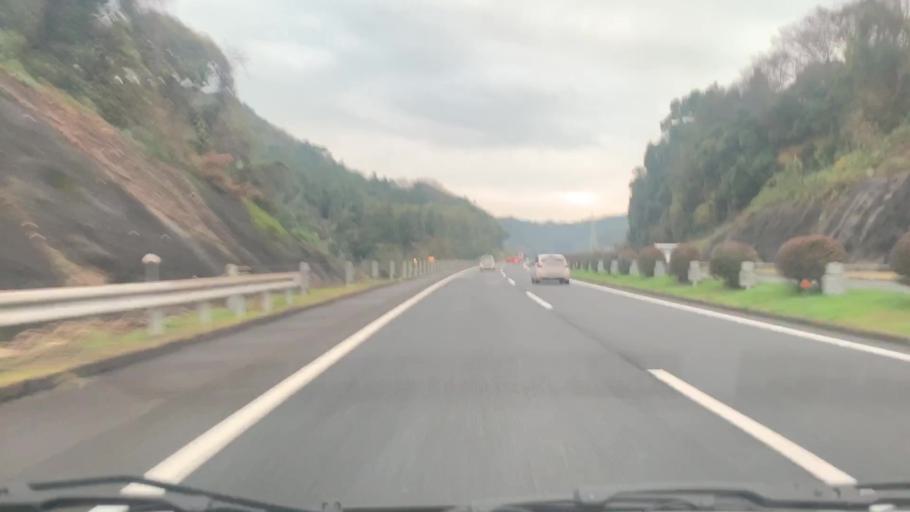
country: JP
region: Nagasaki
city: Omura
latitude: 32.8843
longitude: 129.9951
